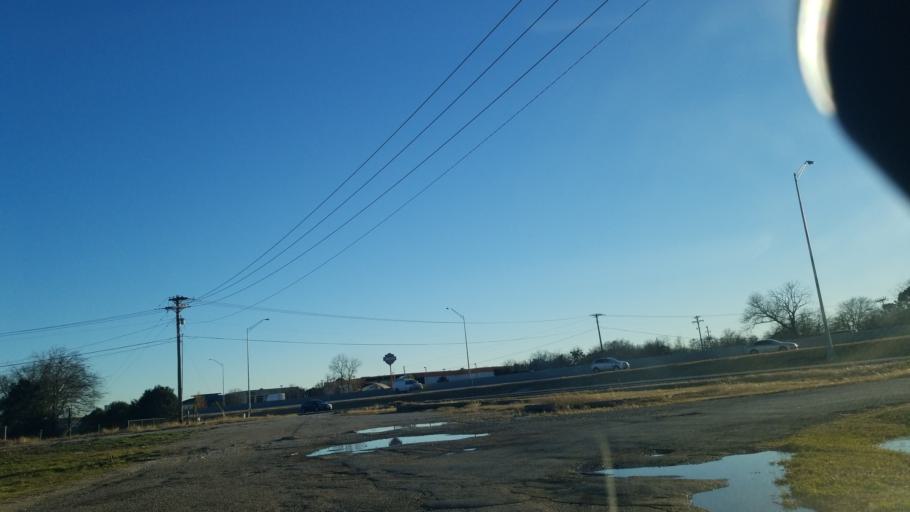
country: US
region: Texas
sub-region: Denton County
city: Corinth
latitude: 33.1554
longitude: -97.0628
